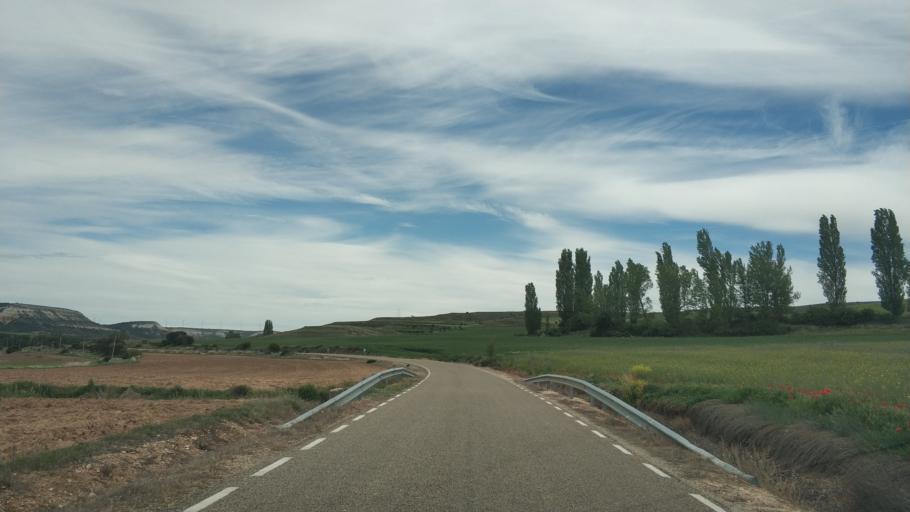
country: ES
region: Castille and Leon
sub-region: Provincia de Soria
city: Berlanga de Duero
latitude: 41.4365
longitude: -2.8134
